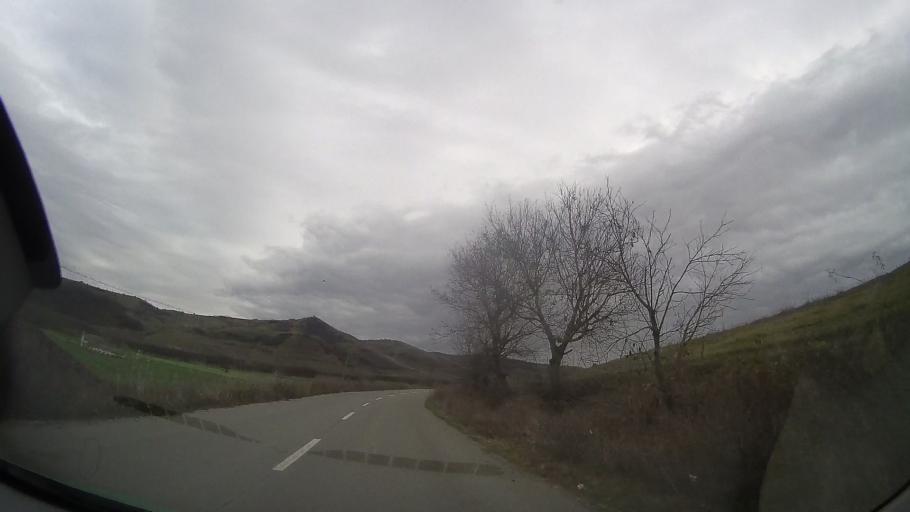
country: RO
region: Mures
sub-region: Comuna Craesti
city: Craiesti
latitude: 46.7829
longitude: 24.4261
